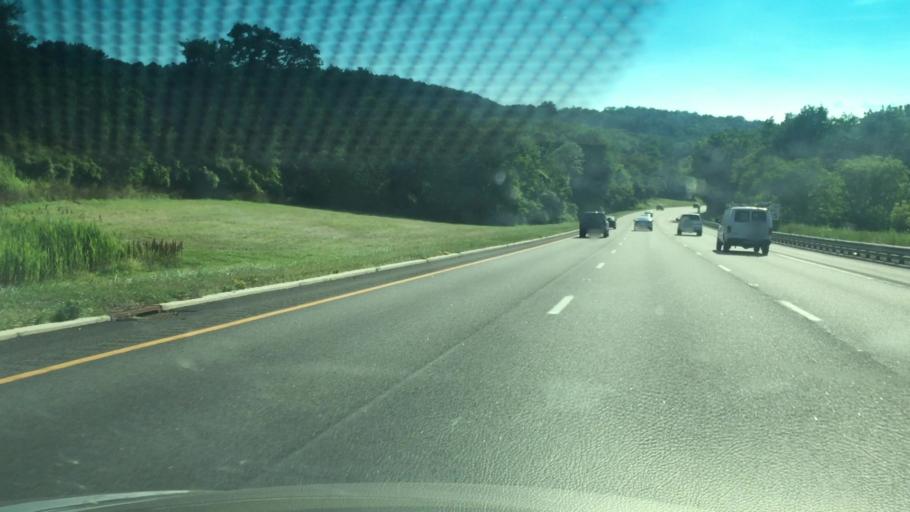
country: US
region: New Jersey
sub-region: Warren County
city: Hackettstown
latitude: 40.9183
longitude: -74.8219
